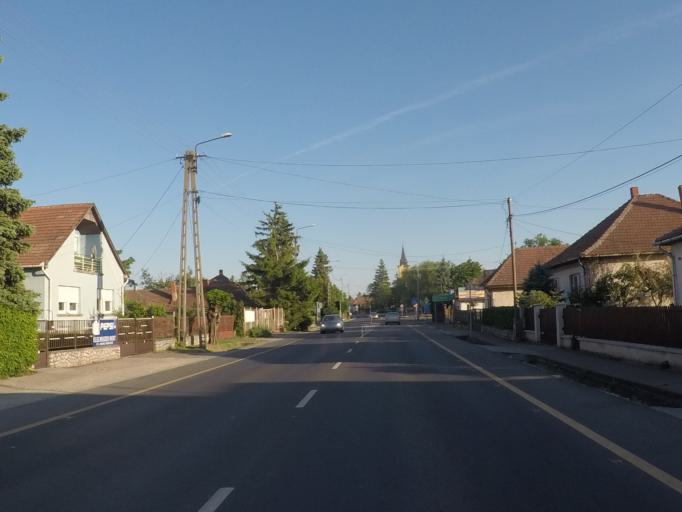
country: HU
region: Heves
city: Besenyotelek
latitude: 47.7224
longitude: 20.4179
